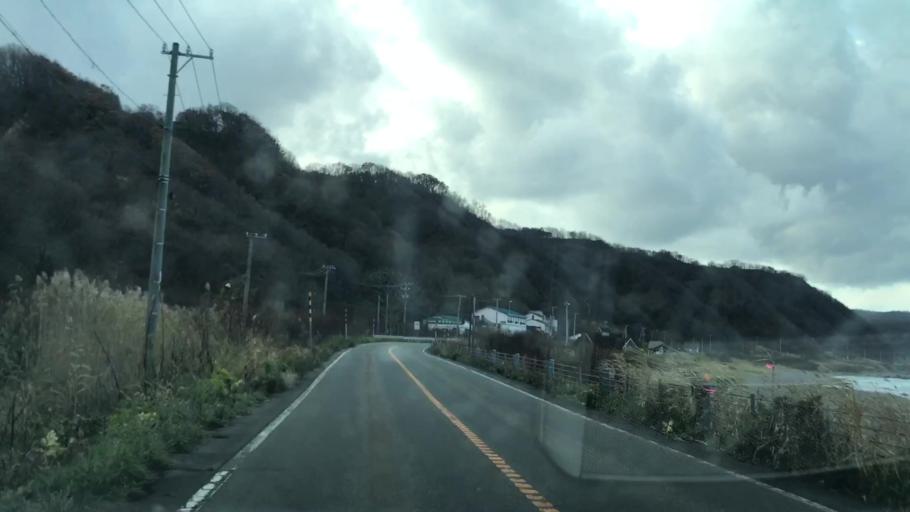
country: JP
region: Hokkaido
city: Yoichi
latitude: 43.3358
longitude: 140.4472
